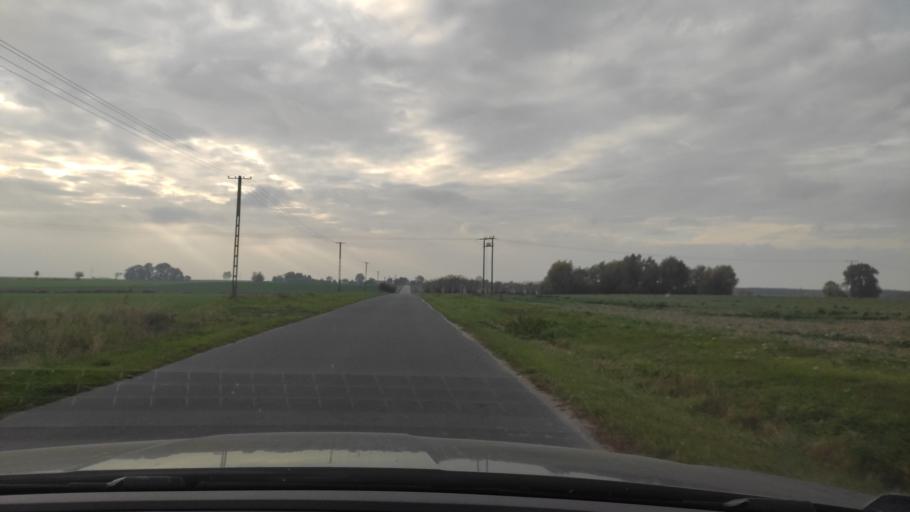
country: PL
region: Greater Poland Voivodeship
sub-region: Powiat poznanski
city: Kostrzyn
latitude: 52.4438
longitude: 17.1918
